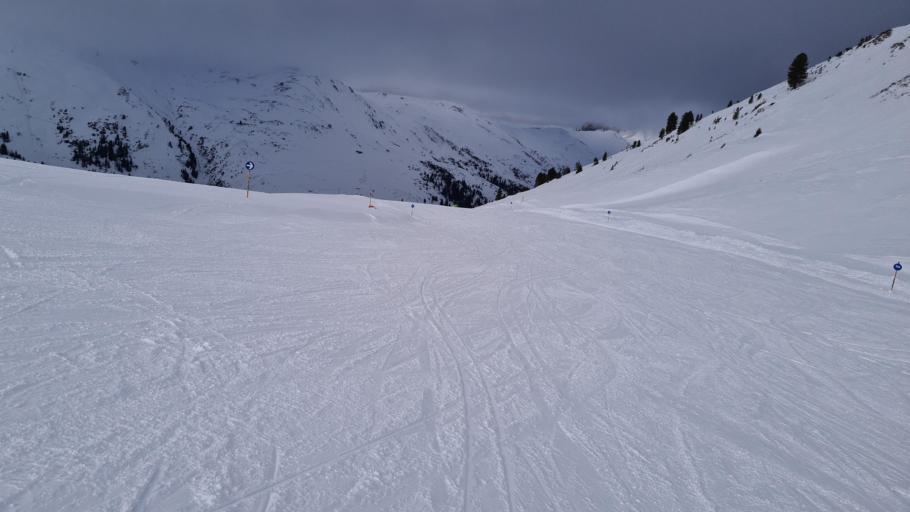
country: AT
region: Salzburg
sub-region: Politischer Bezirk Zell am See
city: Neukirchen am Grossvenediger
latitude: 47.2912
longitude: 12.2935
